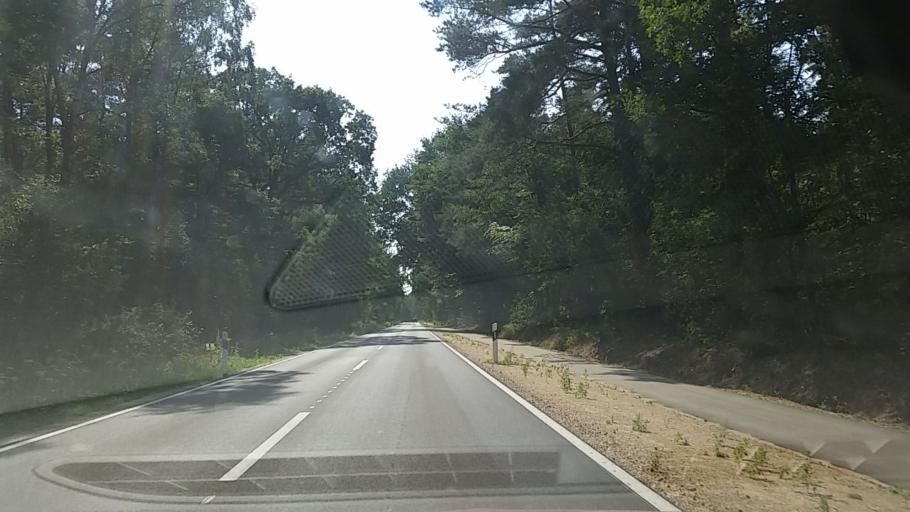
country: DE
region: Schleswig-Holstein
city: Wohltorf
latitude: 53.5567
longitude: 10.2692
